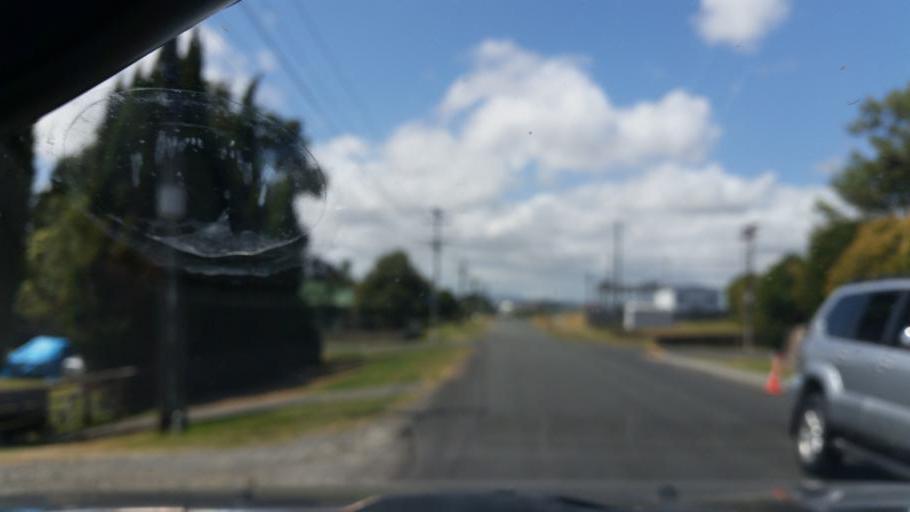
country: NZ
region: Northland
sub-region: Kaipara District
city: Dargaville
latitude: -35.9334
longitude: 173.8770
